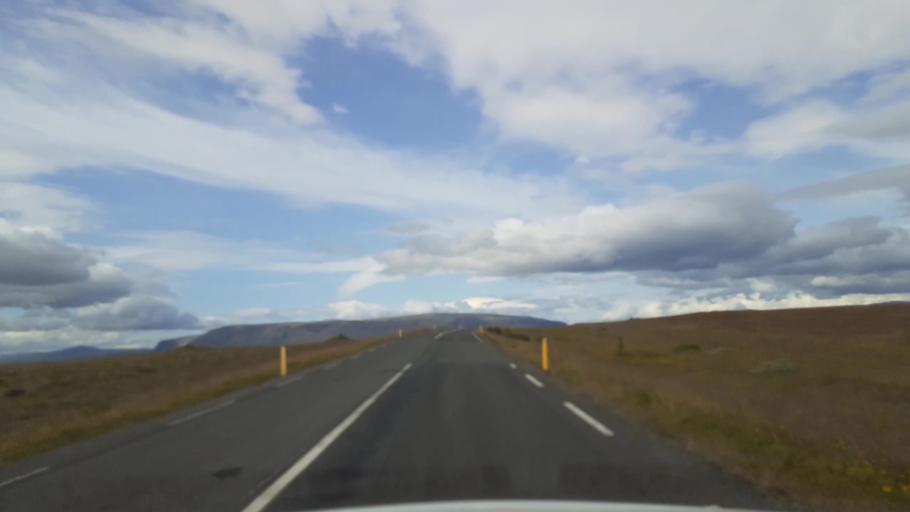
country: IS
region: South
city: Selfoss
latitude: 63.9191
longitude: -20.8472
